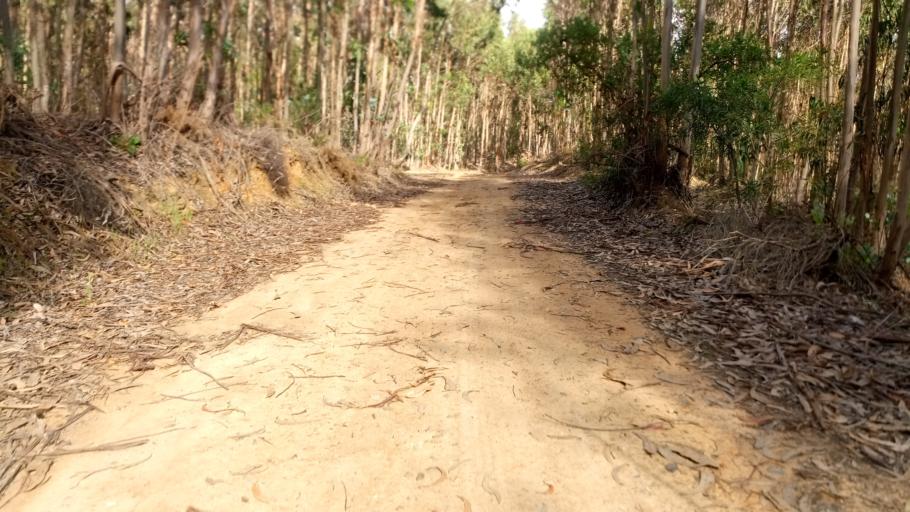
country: PT
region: Leiria
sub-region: Obidos
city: Obidos
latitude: 39.3892
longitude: -9.2133
